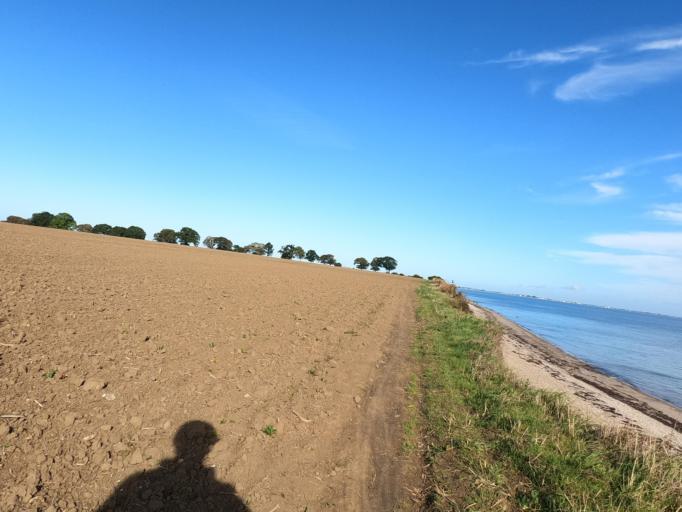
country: DE
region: Schleswig-Holstein
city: Dahme
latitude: 54.2850
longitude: 11.0817
